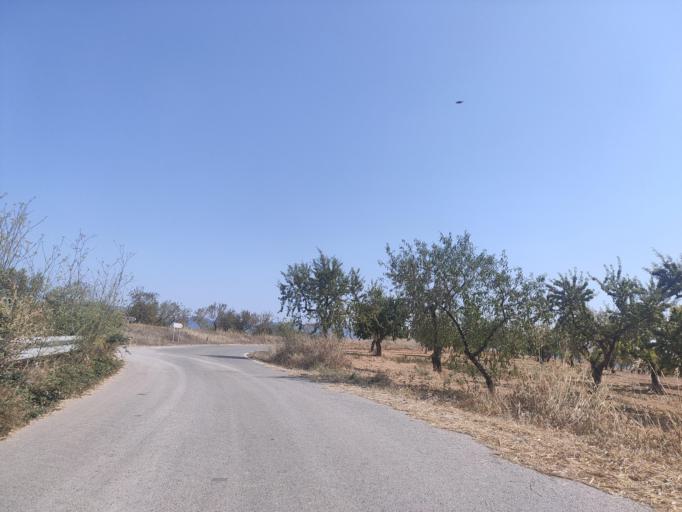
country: ES
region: Aragon
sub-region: Provincia de Teruel
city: Lledo
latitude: 40.9256
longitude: 0.2205
